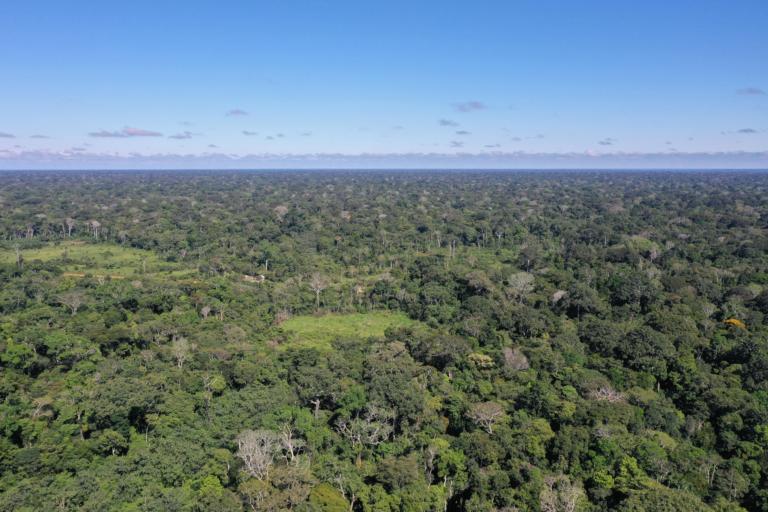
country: PE
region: Madre de Dios
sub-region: Provincia de Tambopata
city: Puerto Maldonado
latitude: -12.2193
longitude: -68.6169
